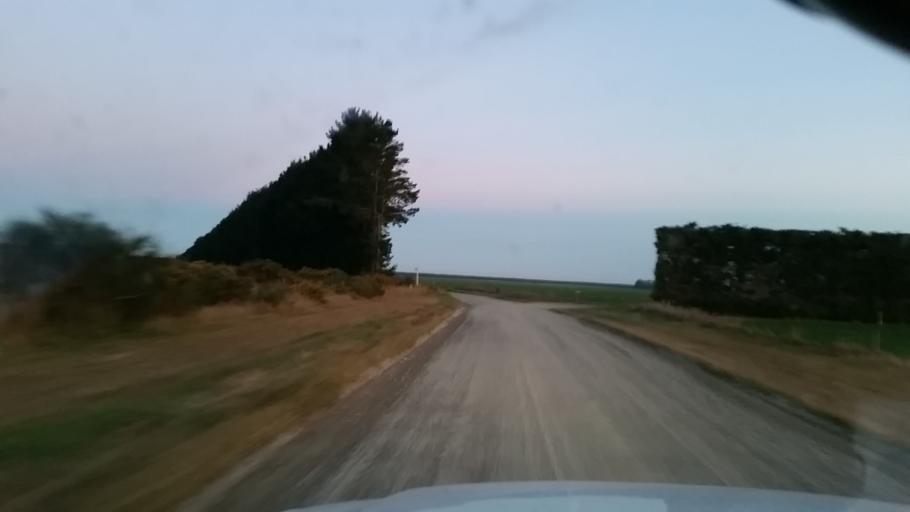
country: NZ
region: Canterbury
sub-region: Ashburton District
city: Tinwald
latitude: -43.9453
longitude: 171.6110
